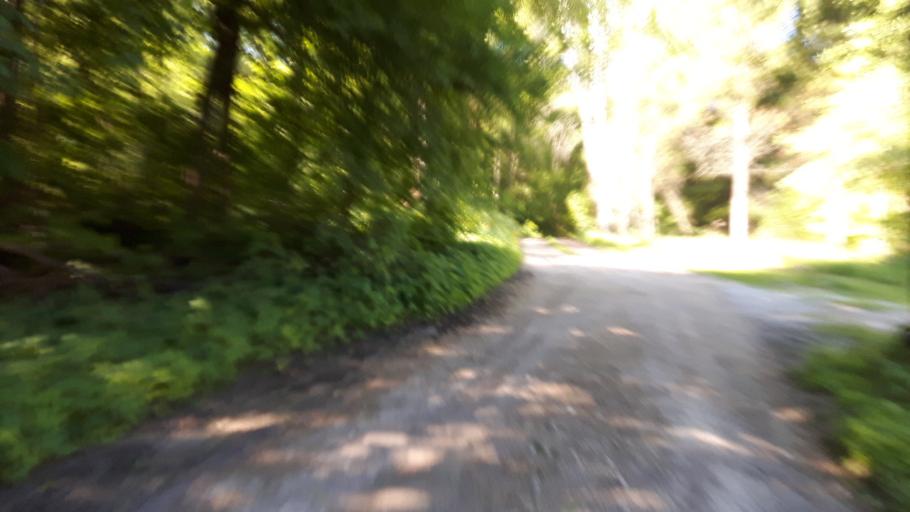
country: EE
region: Harju
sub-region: Loksa linn
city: Loksa
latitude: 59.5654
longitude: 25.8410
